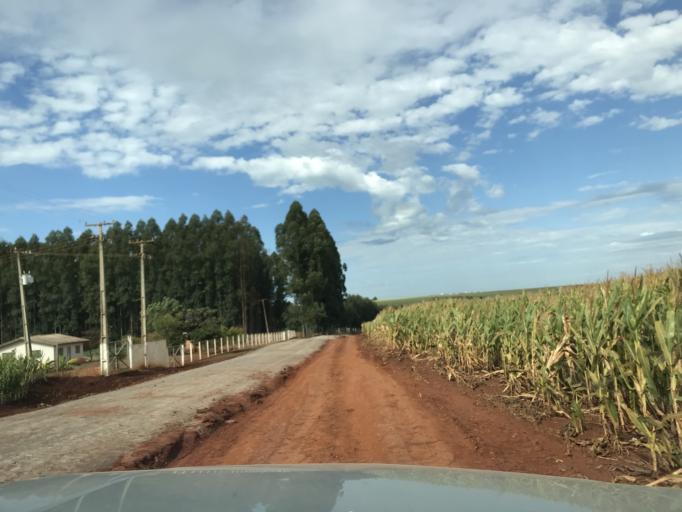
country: BR
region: Parana
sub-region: Palotina
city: Palotina
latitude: -24.2986
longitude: -53.8134
